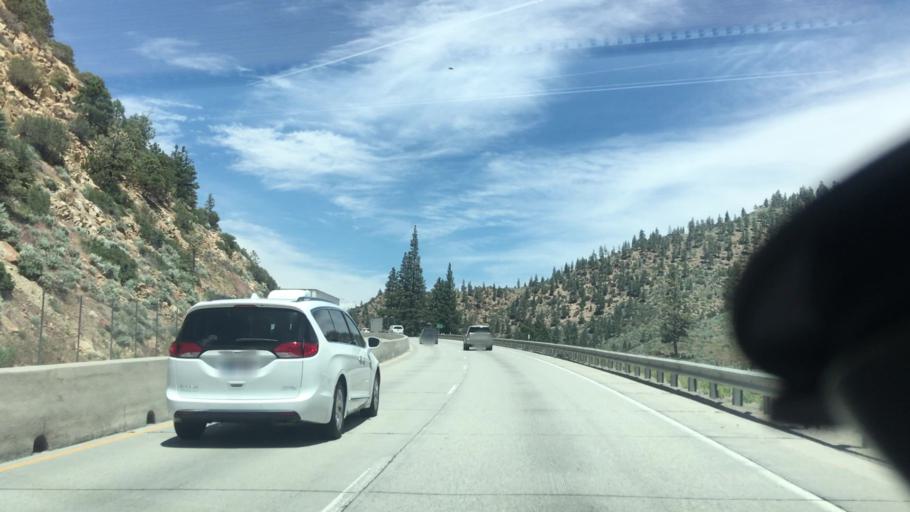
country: US
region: Nevada
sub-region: Washoe County
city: Verdi
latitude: 39.4438
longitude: -120.0111
